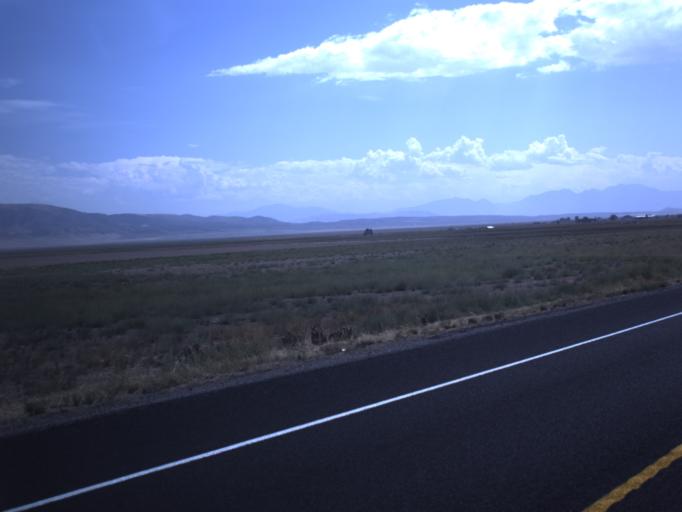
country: US
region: Utah
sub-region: Utah County
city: Eagle Mountain
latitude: 40.2831
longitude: -112.0960
